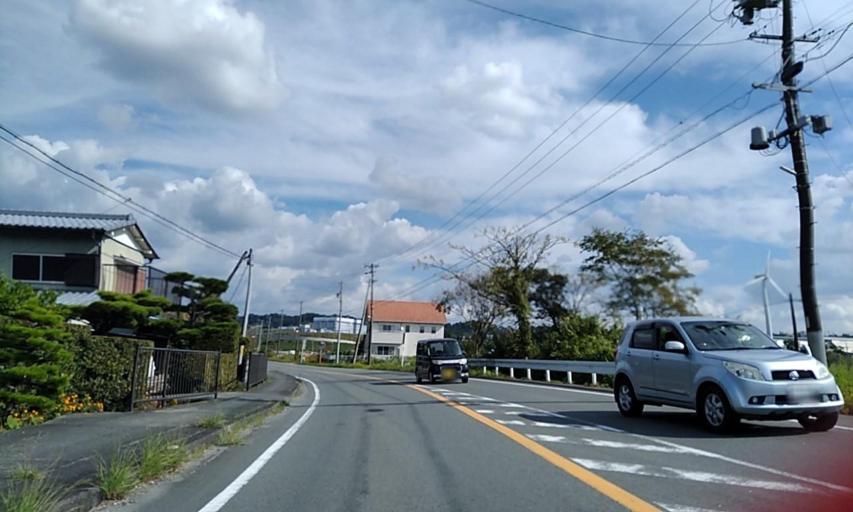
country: JP
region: Shizuoka
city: Hamakita
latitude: 34.8362
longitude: 137.8475
